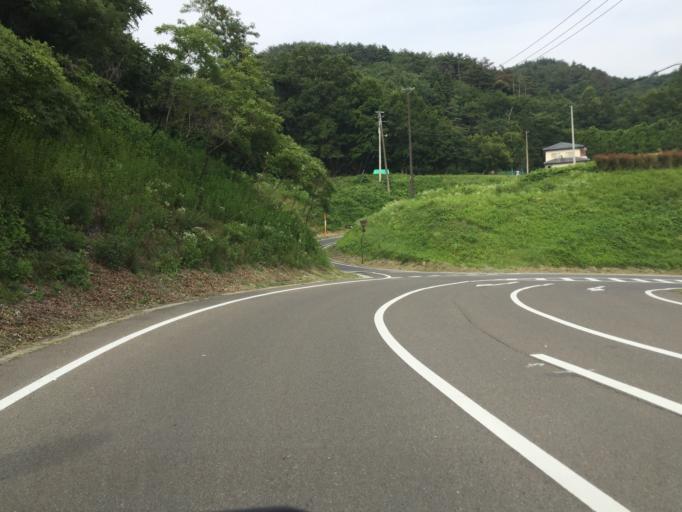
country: JP
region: Fukushima
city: Fukushima-shi
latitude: 37.7310
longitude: 140.4792
